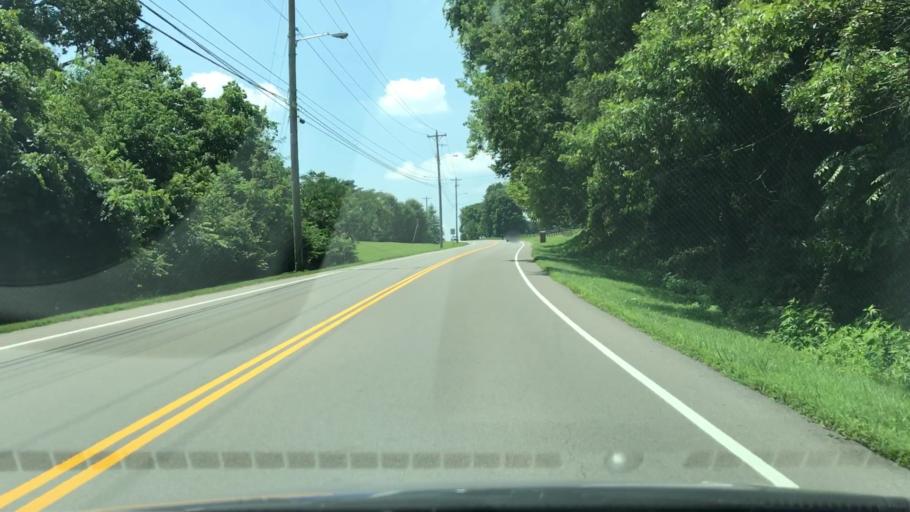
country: US
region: Tennessee
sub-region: Williamson County
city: Brentwood Estates
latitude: 35.9977
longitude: -86.7436
